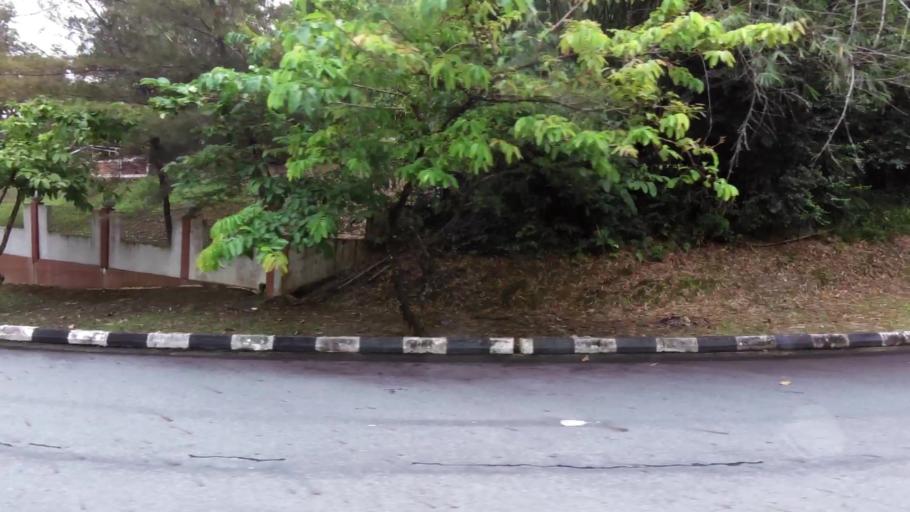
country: BN
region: Brunei and Muara
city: Bandar Seri Begawan
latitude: 4.8841
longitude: 114.9315
